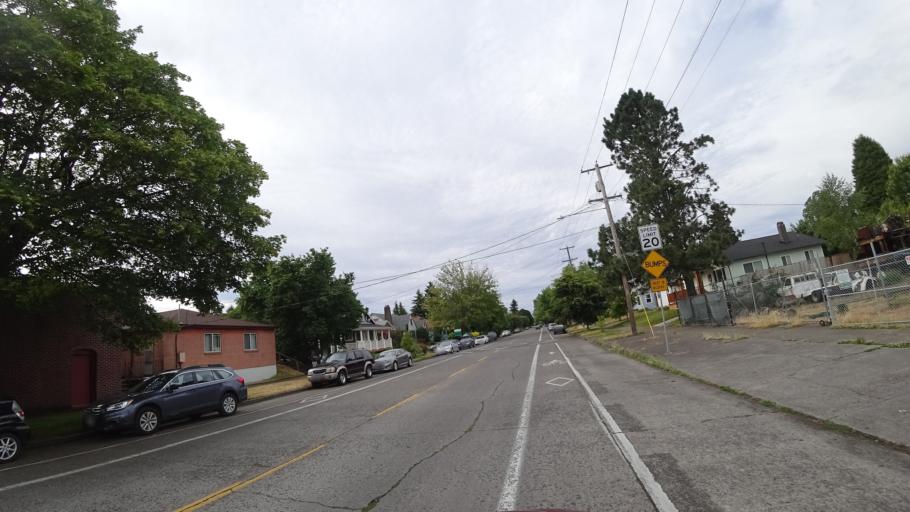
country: US
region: Oregon
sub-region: Multnomah County
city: Portland
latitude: 45.5628
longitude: -122.6875
